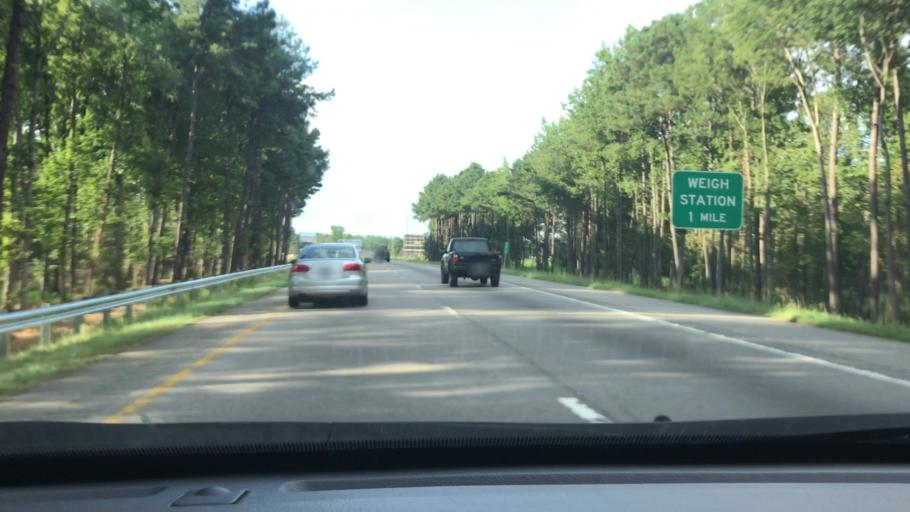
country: US
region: North Carolina
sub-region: Robeson County
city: Lumberton
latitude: 34.6899
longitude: -78.9992
